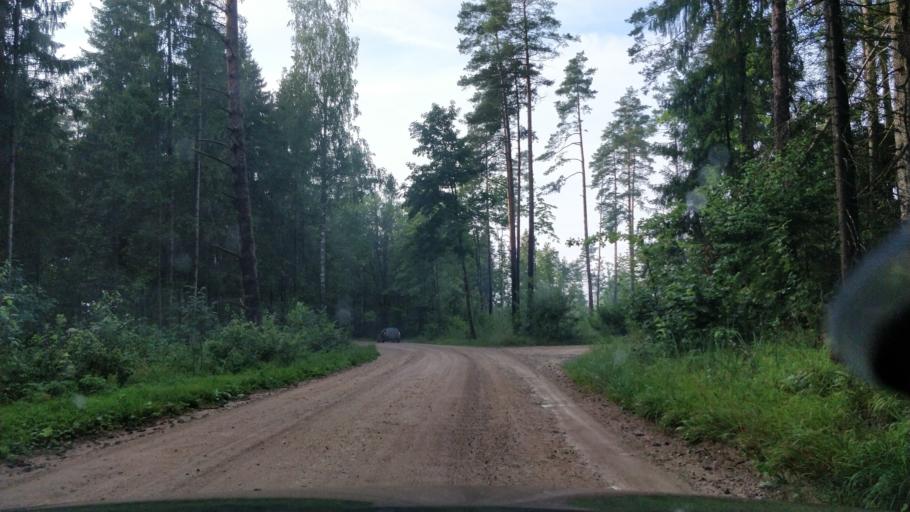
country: LV
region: Incukalns
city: Incukalns
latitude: 57.0928
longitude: 24.7649
